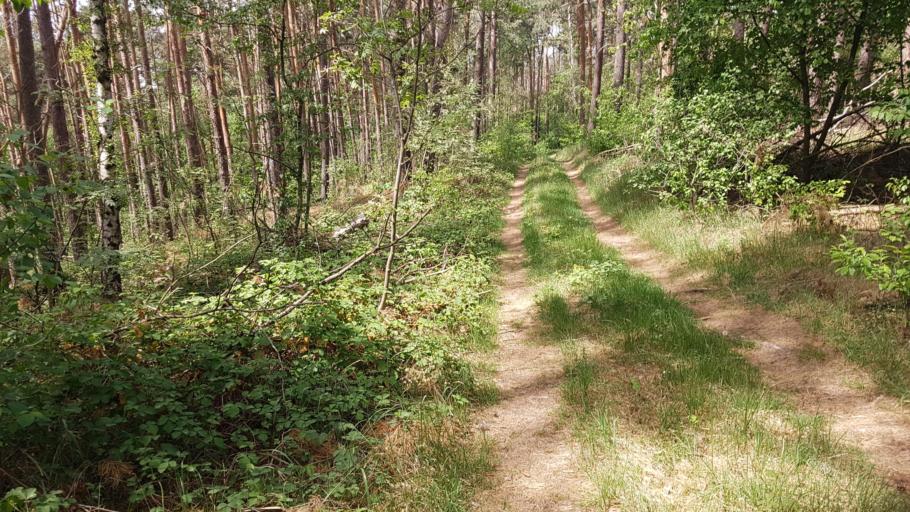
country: DE
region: Brandenburg
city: Grosskmehlen
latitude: 51.3707
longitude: 13.7052
